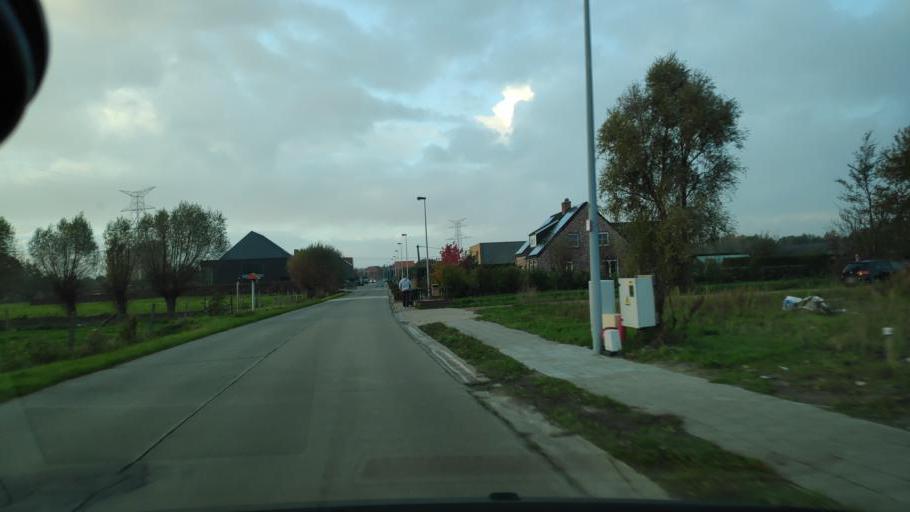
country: BE
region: Flanders
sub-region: Provincie West-Vlaanderen
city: Zedelgem
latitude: 51.1432
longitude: 3.1265
